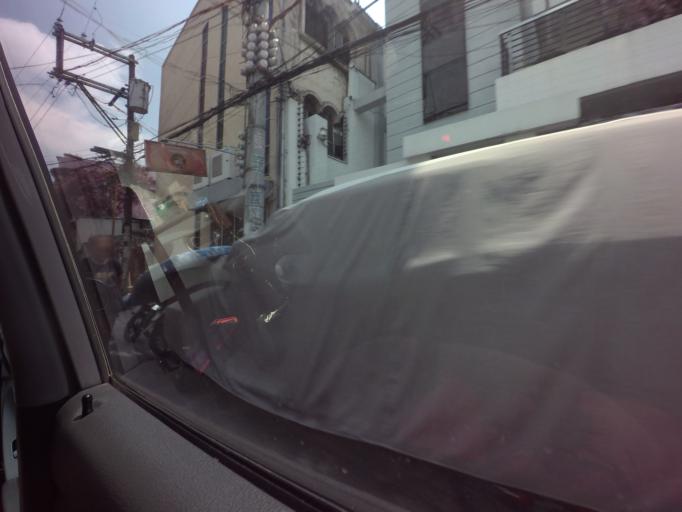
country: PH
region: Metro Manila
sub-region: City of Manila
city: Quiapo
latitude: 14.5900
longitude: 121.0028
